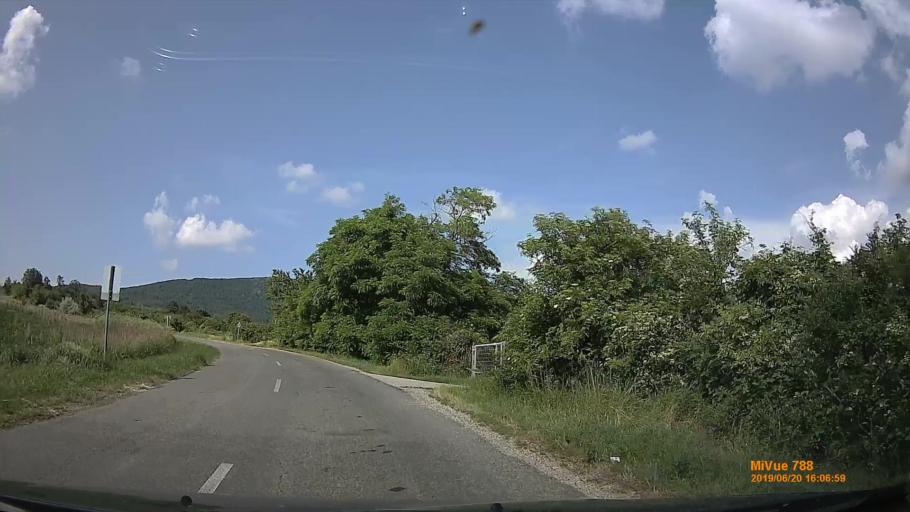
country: HU
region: Baranya
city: Pellerd
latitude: 46.0836
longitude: 18.1116
